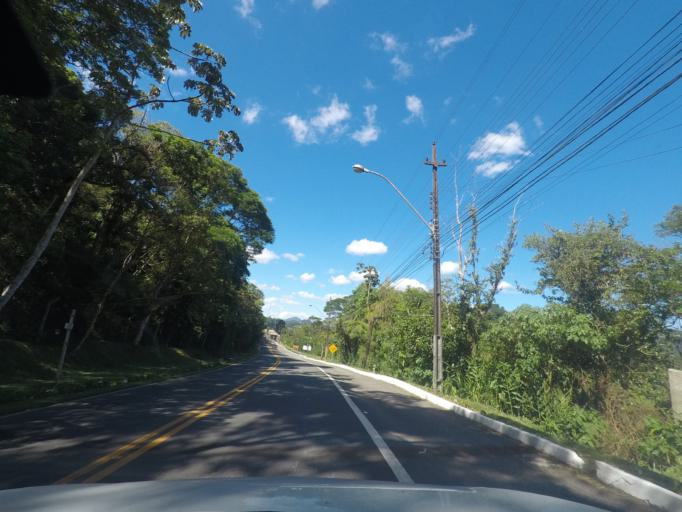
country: BR
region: Rio de Janeiro
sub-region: Teresopolis
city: Teresopolis
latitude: -22.4582
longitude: -42.9862
